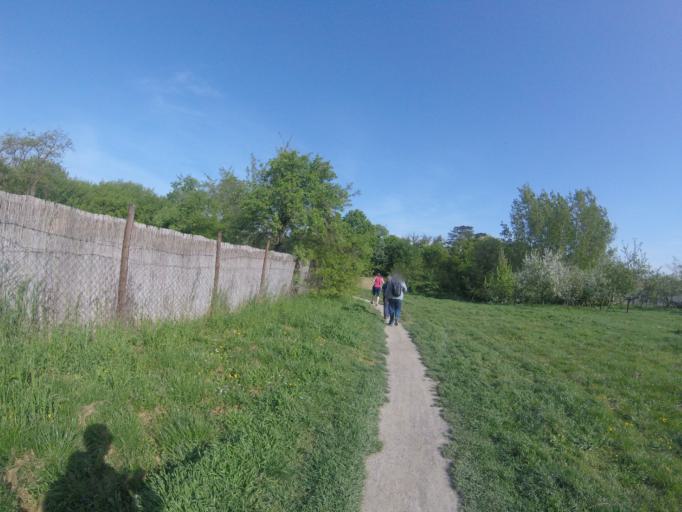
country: HU
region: Bekes
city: Doboz
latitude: 46.7370
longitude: 21.2461
